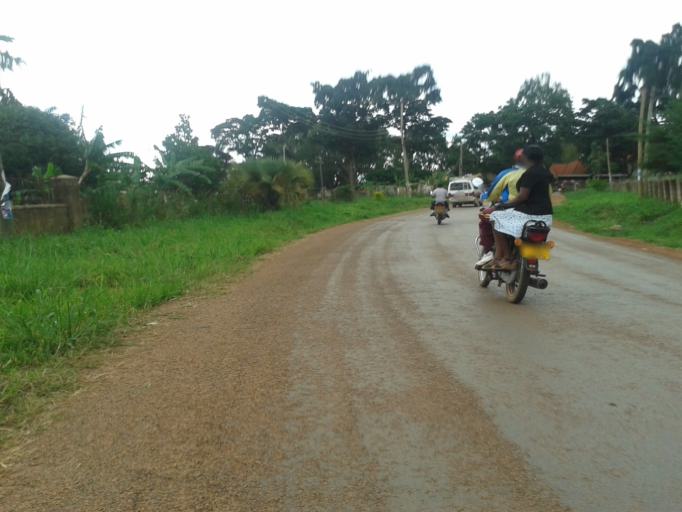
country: UG
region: Northern Region
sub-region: Gulu District
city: Gulu
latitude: 2.7792
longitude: 32.2986
